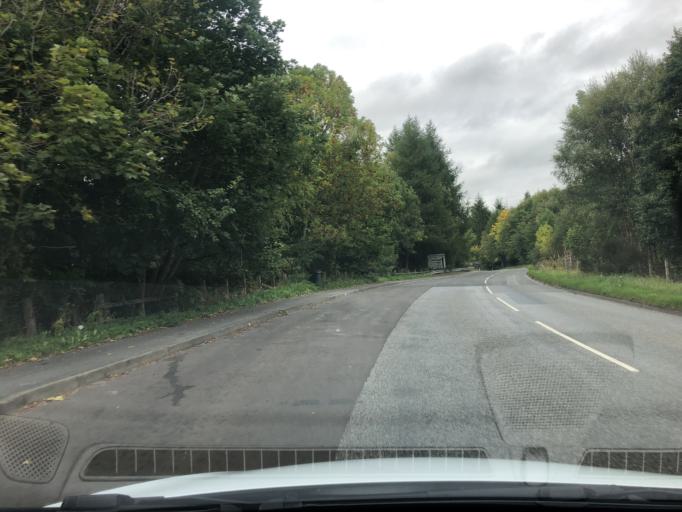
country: GB
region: Scotland
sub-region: Perth and Kinross
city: Pitlochry
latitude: 56.7261
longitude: -3.7749
